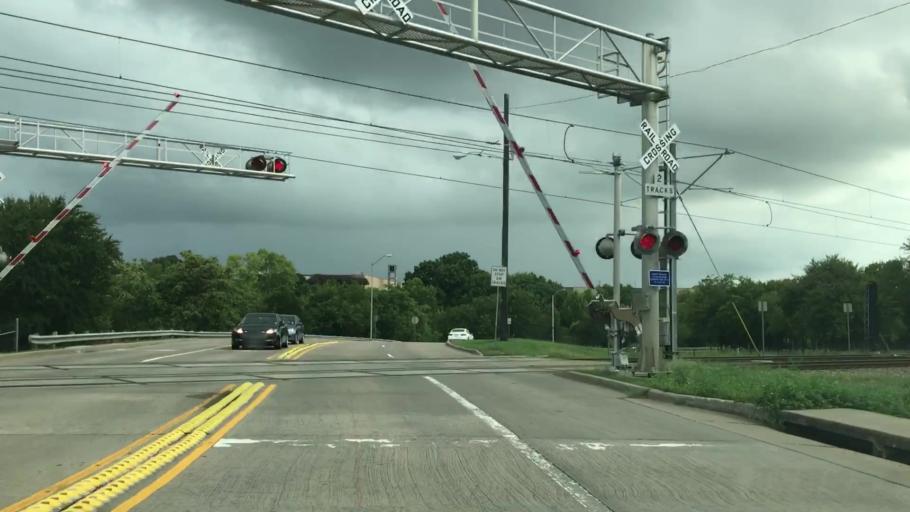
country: US
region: Texas
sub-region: Dallas County
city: Richardson
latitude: 32.9163
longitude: -96.7545
